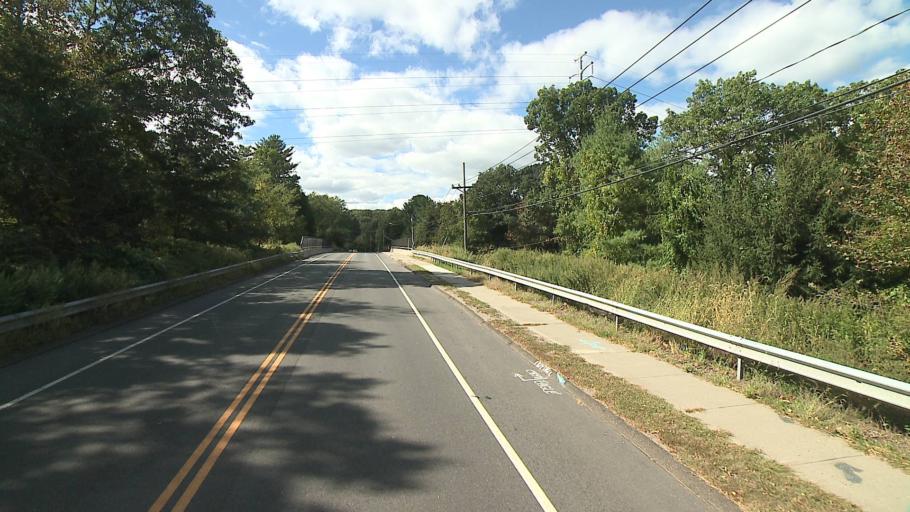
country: US
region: Connecticut
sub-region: Fairfield County
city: Wilton
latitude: 41.1827
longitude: -73.4218
